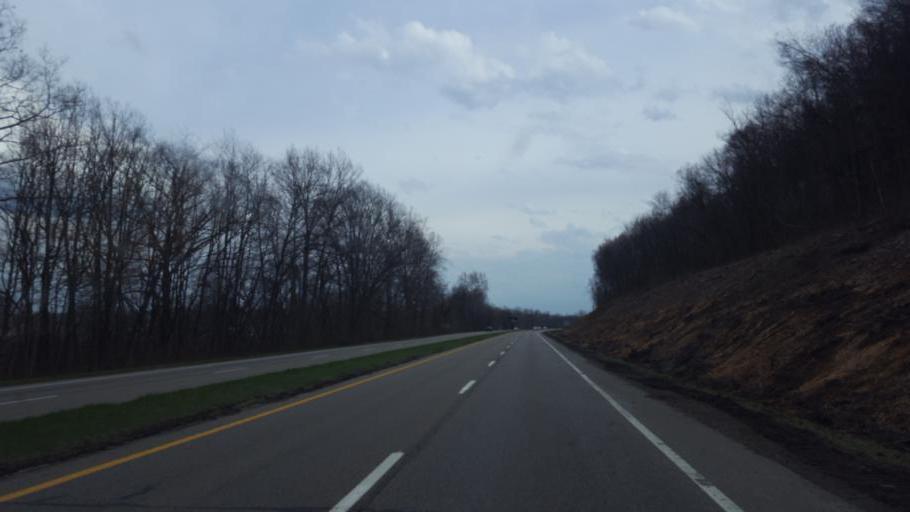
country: US
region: Ohio
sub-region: Coshocton County
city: Coshocton
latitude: 40.2651
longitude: -81.8752
